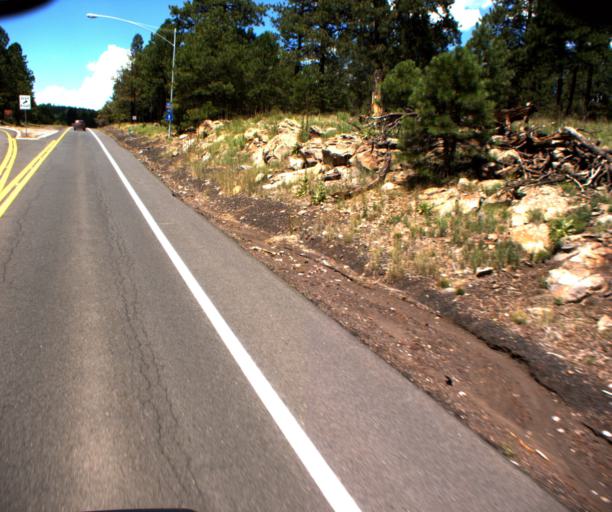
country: US
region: Arizona
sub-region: Coconino County
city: Flagstaff
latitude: 35.1928
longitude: -111.7266
